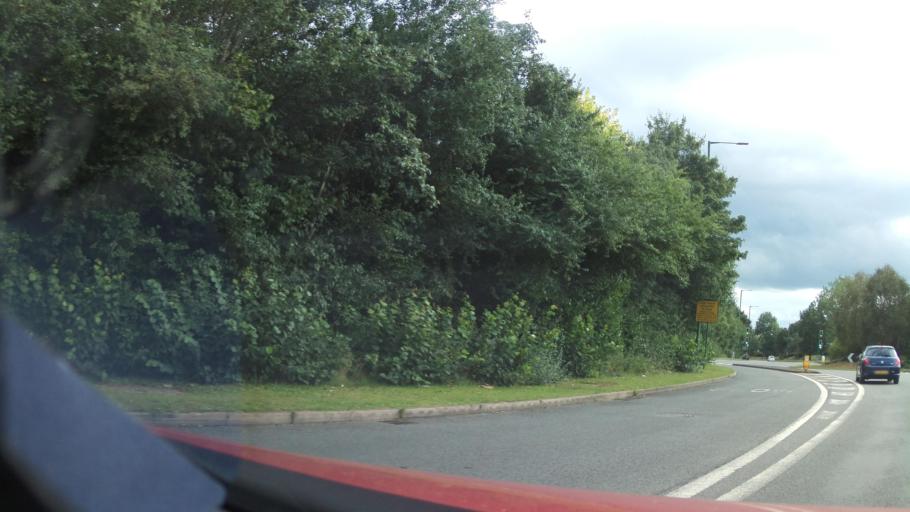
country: GB
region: England
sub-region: Solihull
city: Bickenhill
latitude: 52.4599
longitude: -1.7270
